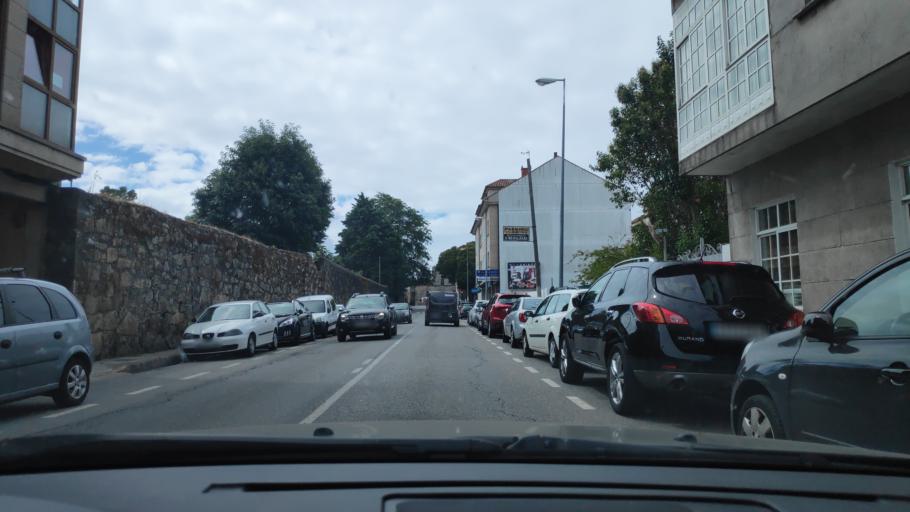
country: ES
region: Galicia
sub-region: Provincia de Pontevedra
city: Cambados
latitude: 42.5211
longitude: -8.8130
